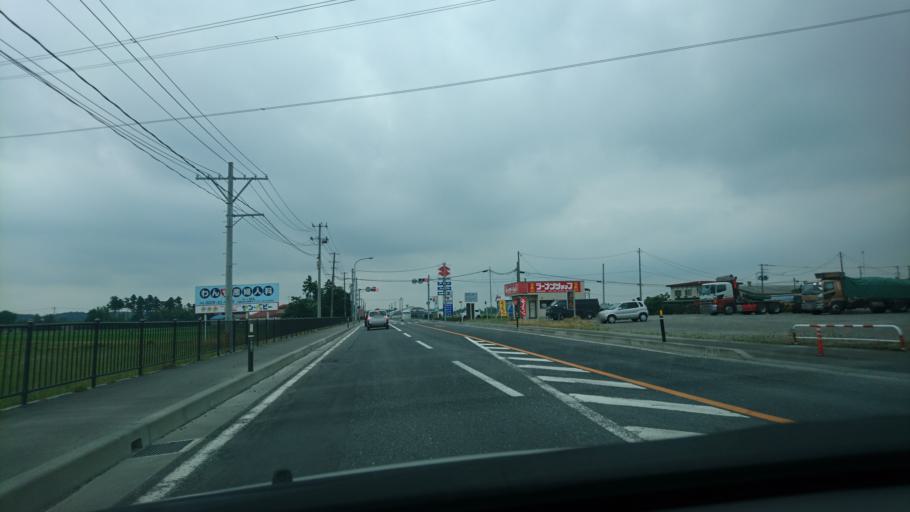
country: JP
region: Miyagi
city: Furukawa
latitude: 38.6330
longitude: 140.8930
